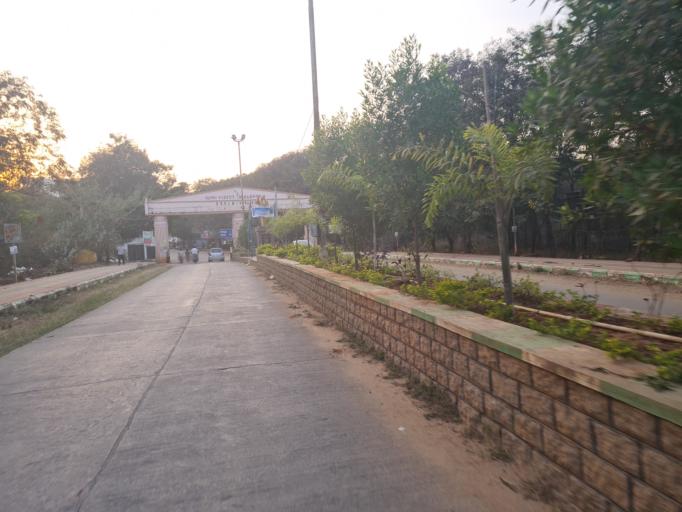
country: IN
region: Telangana
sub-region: Medak
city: Serilingampalle
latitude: 17.4780
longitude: 78.2915
